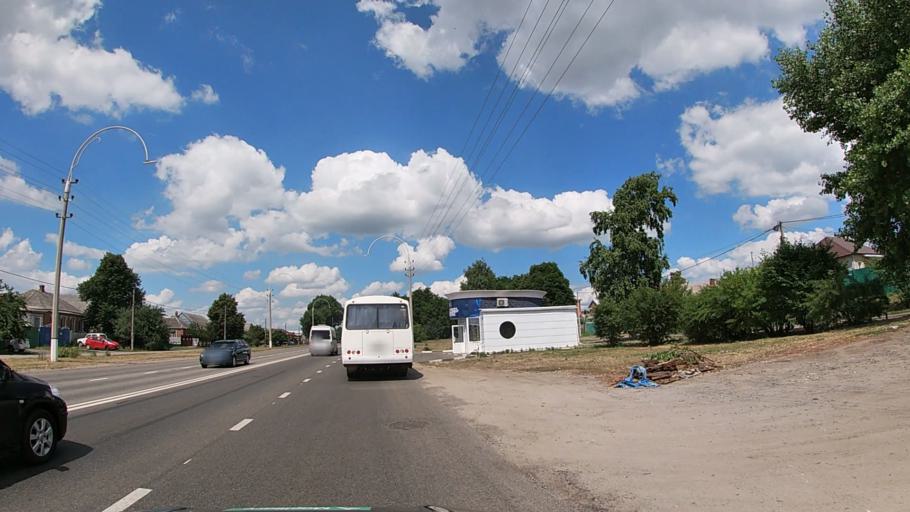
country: RU
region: Belgorod
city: Severnyy
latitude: 50.6256
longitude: 36.4982
